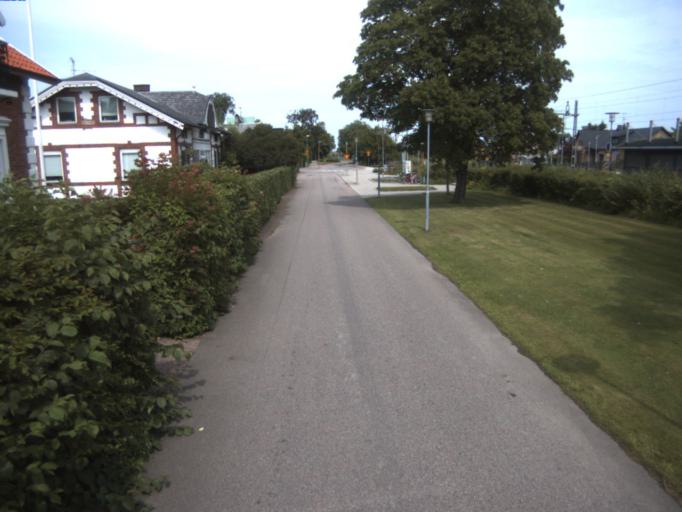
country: SE
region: Skane
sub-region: Helsingborg
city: Odakra
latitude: 56.1048
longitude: 12.7447
